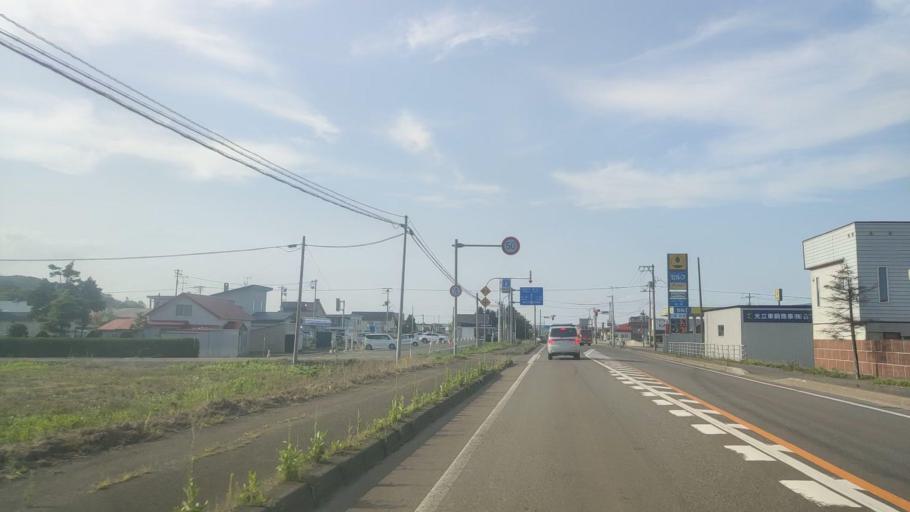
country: JP
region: Hokkaido
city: Iwamizawa
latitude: 43.0071
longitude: 141.7897
